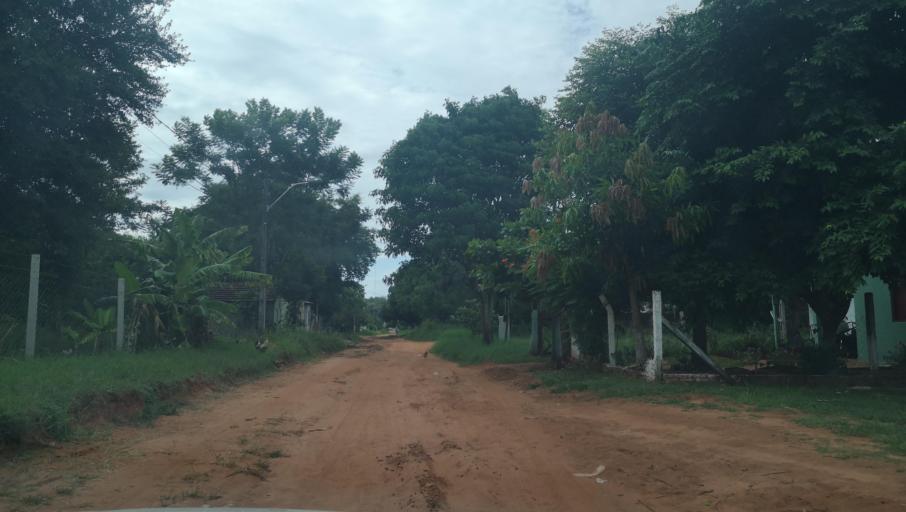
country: PY
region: San Pedro
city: Capiibary
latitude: -24.7254
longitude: -56.0225
